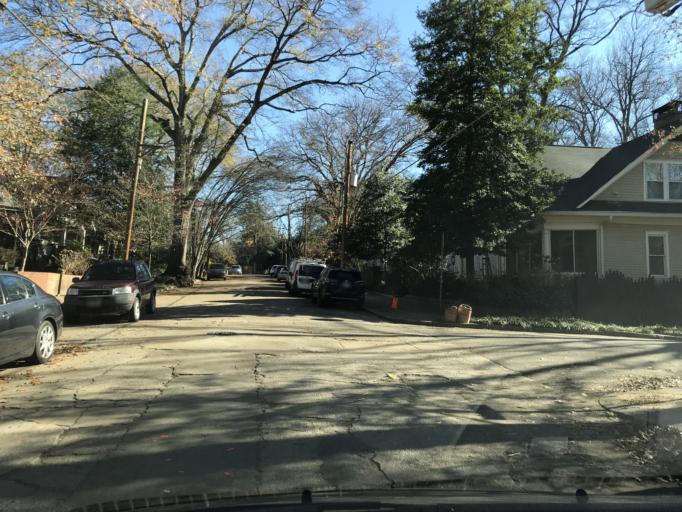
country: US
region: Georgia
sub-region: Fulton County
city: Atlanta
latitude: 33.7579
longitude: -84.3603
